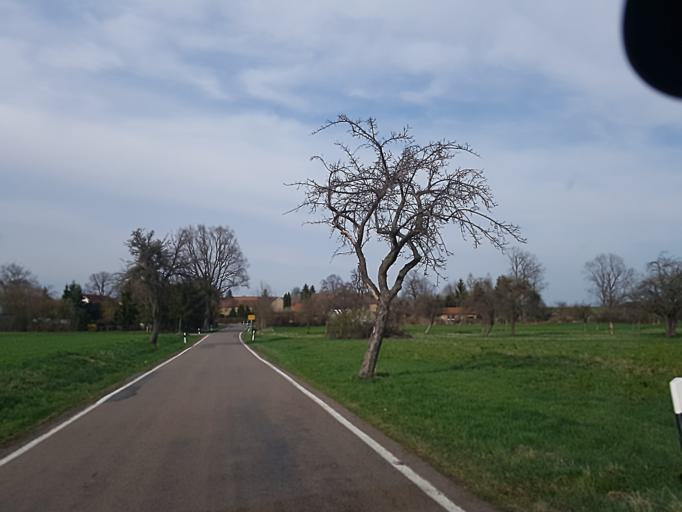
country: DE
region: Saxony
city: Strehla
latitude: 51.3650
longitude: 13.1930
